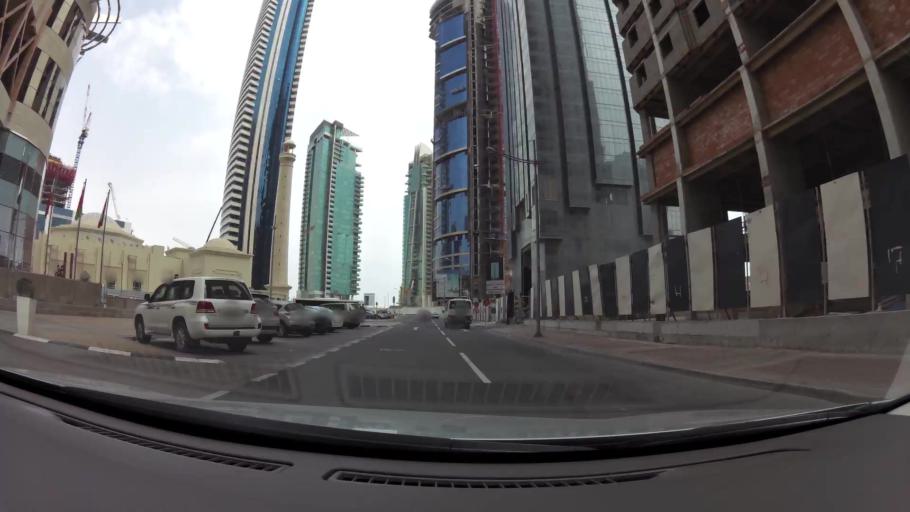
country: QA
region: Baladiyat ad Dawhah
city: Doha
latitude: 25.3284
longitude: 51.5334
